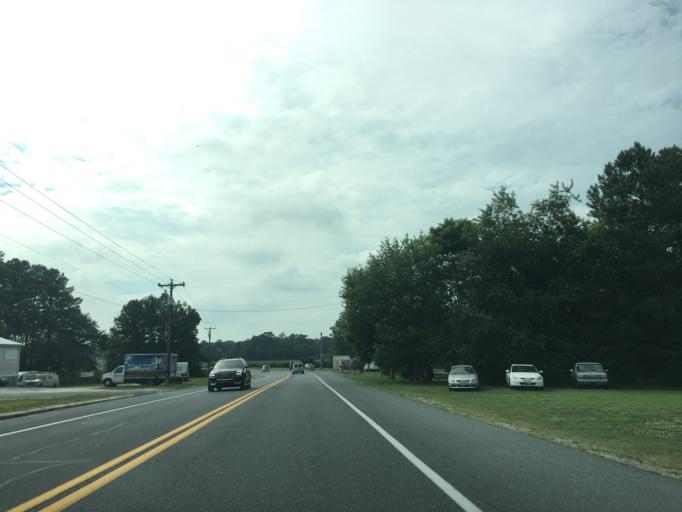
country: US
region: Delaware
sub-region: Sussex County
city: Long Neck
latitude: 38.5560
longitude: -75.1982
